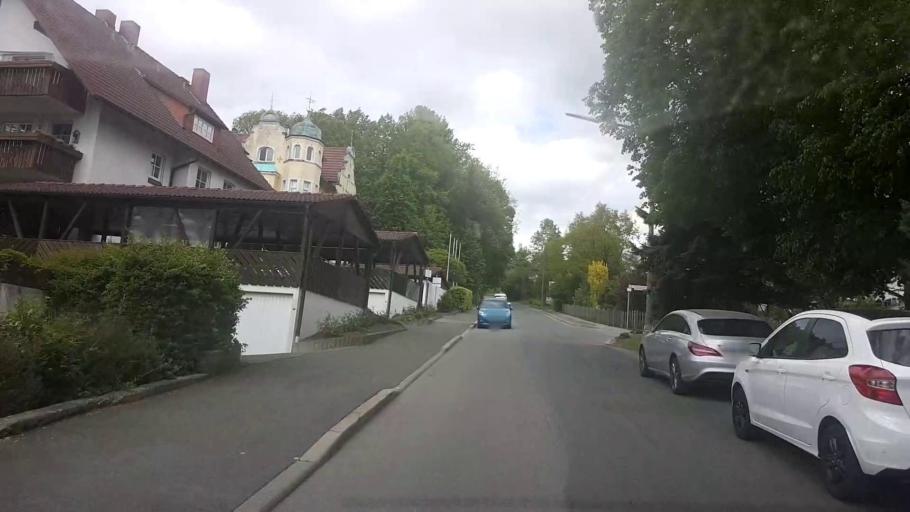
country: DE
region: Bavaria
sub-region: Upper Franconia
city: Lichtenfels
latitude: 50.1564
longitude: 11.0565
